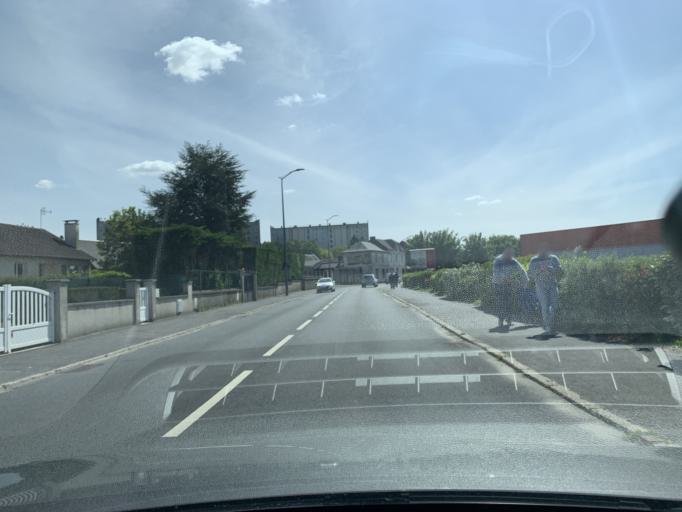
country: FR
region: Picardie
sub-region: Departement de l'Aisne
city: Saint-Quentin
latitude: 49.8624
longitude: 3.2915
